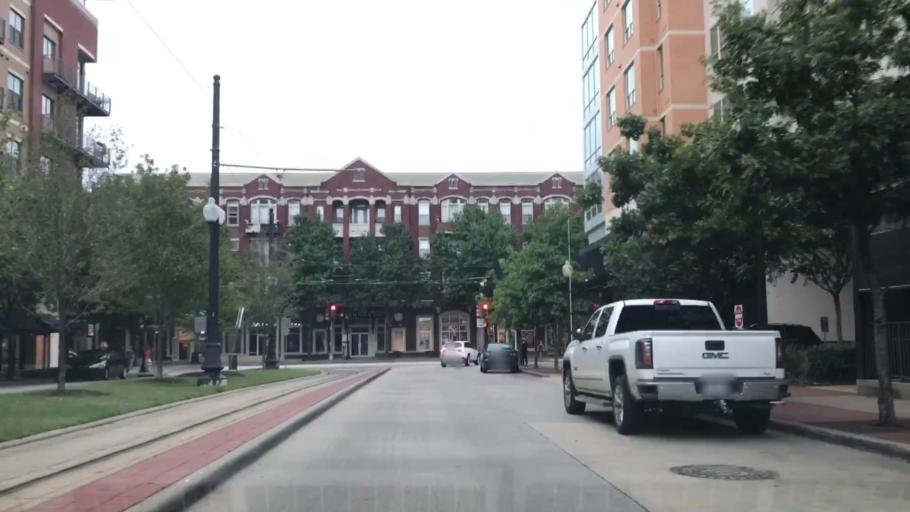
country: US
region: Texas
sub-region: Dallas County
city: Highland Park
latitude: 32.8075
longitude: -96.7963
